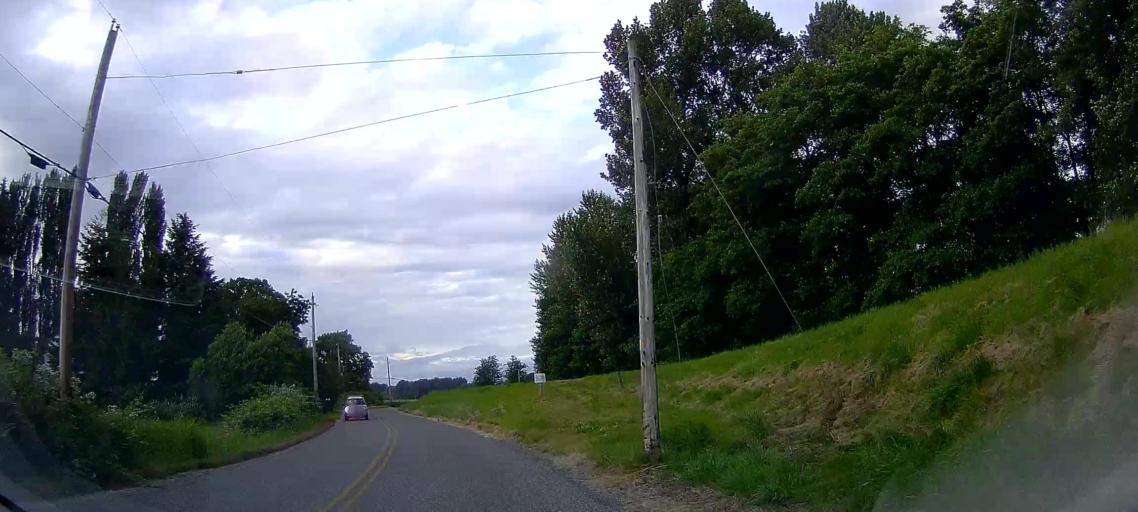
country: US
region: Washington
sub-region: Skagit County
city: Mount Vernon
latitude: 48.3547
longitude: -122.3628
